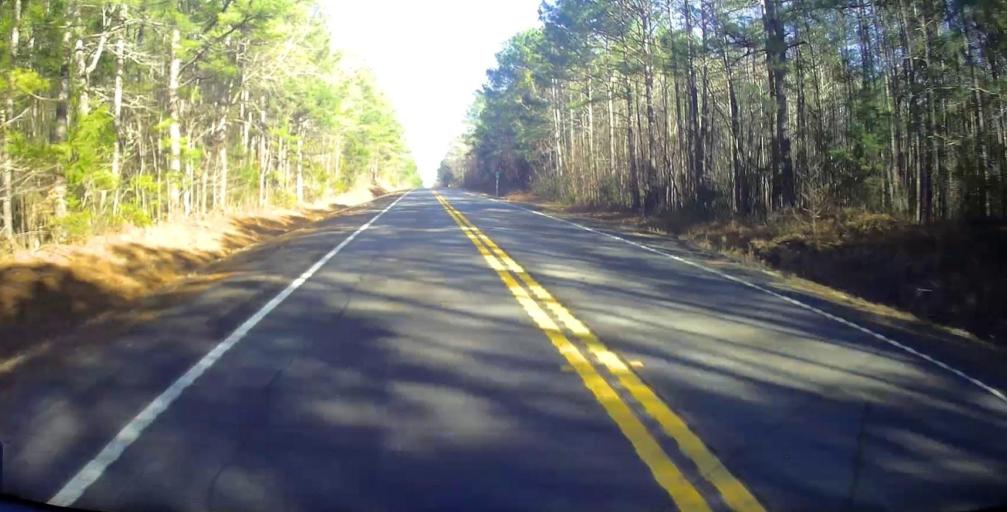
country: US
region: Georgia
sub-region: Talbot County
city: Talbotton
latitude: 32.6725
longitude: -84.5111
